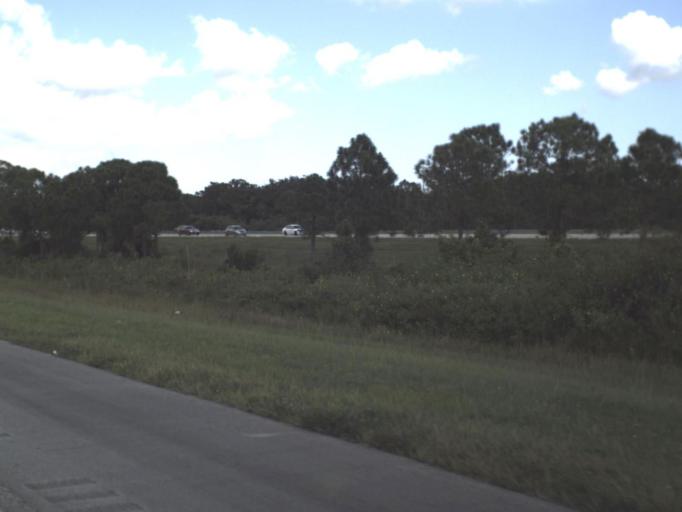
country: US
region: Florida
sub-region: Palm Beach County
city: Limestone Creek
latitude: 26.9695
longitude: -80.1765
